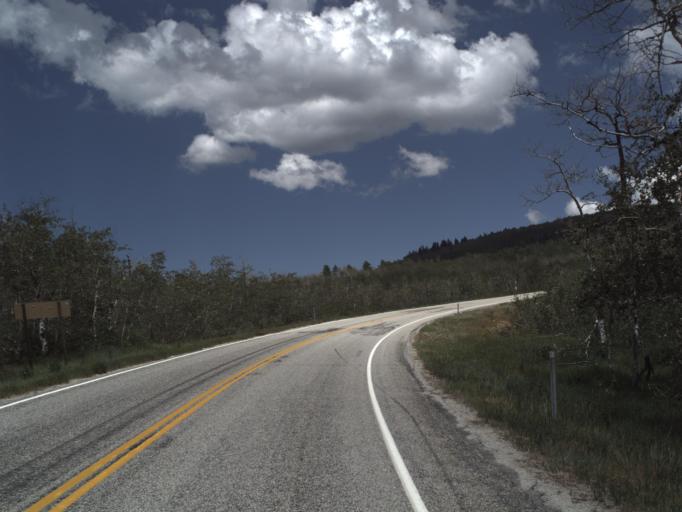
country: US
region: Utah
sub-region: Weber County
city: Wolf Creek
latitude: 41.4077
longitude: -111.5397
